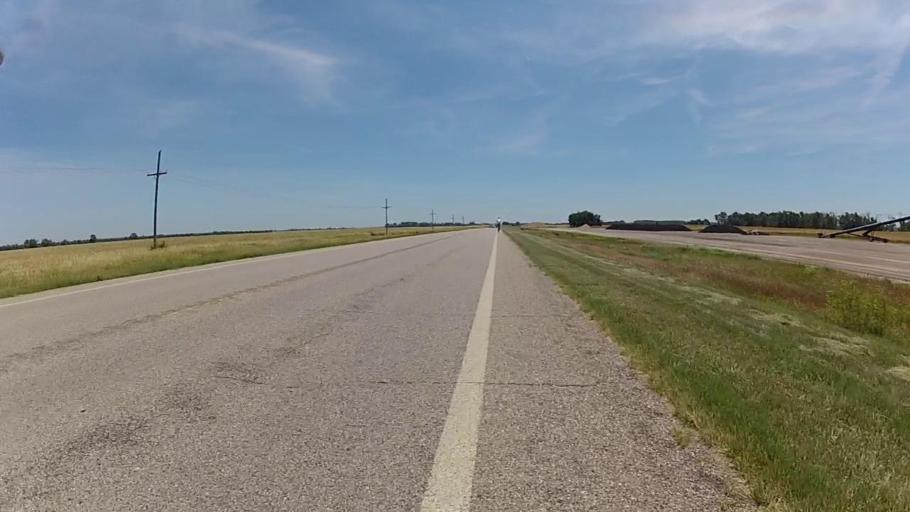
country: US
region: Kansas
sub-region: Barber County
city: Medicine Lodge
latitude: 37.2543
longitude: -98.5116
